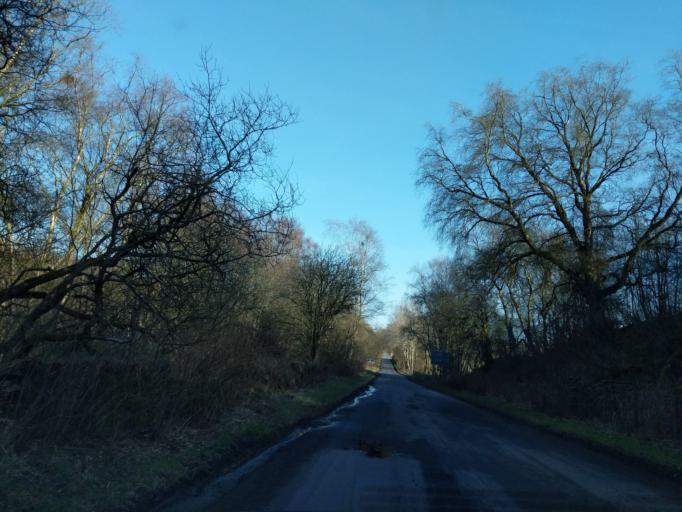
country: GB
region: Scotland
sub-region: The Scottish Borders
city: West Linton
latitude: 55.7194
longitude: -3.4291
